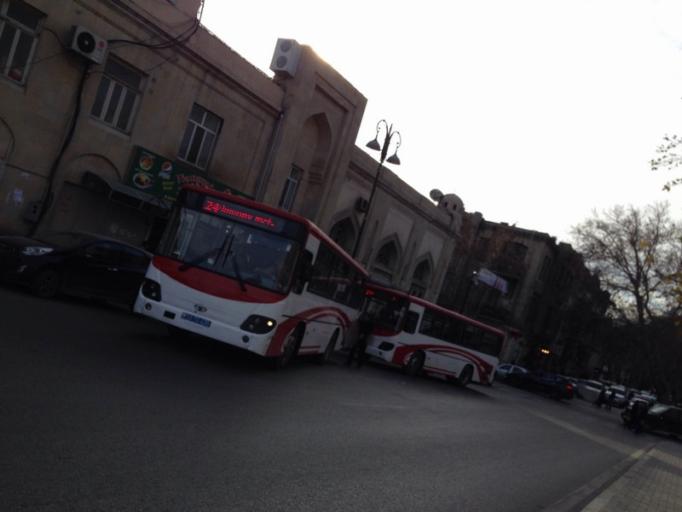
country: AZ
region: Baki
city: Baku
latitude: 40.3808
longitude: 49.8474
